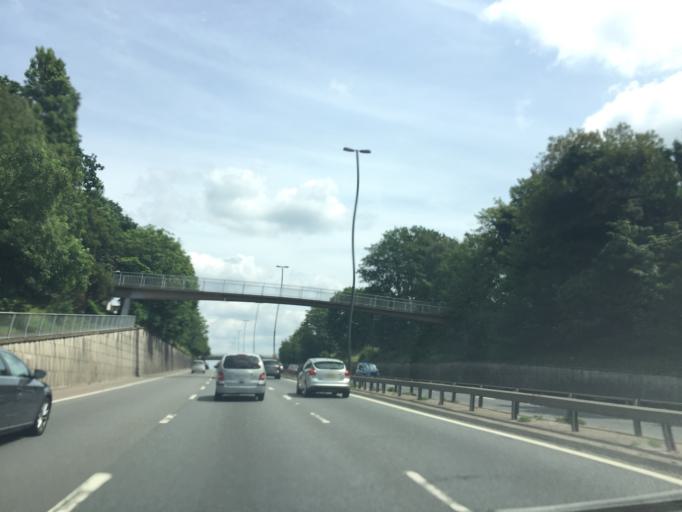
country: GB
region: England
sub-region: Greater London
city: Bexleyheath
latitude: 51.4483
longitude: 0.1315
